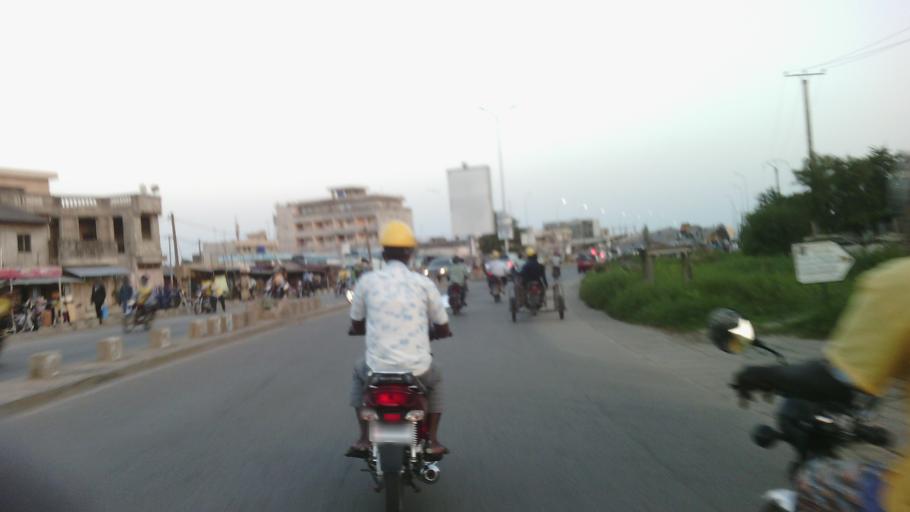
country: BJ
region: Littoral
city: Cotonou
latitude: 6.3717
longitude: 2.3932
